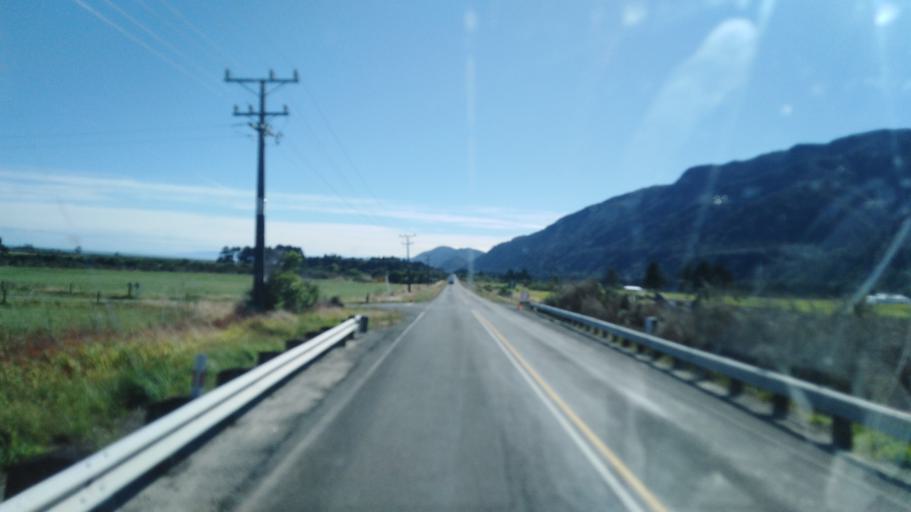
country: NZ
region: West Coast
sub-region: Buller District
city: Westport
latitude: -41.6664
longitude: 171.8104
